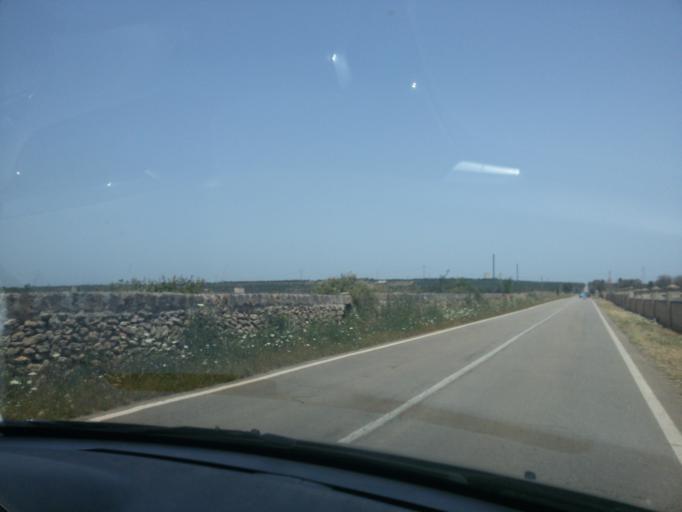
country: IT
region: Apulia
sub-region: Provincia di Lecce
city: Porto Cesareo
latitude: 40.2822
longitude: 17.9074
